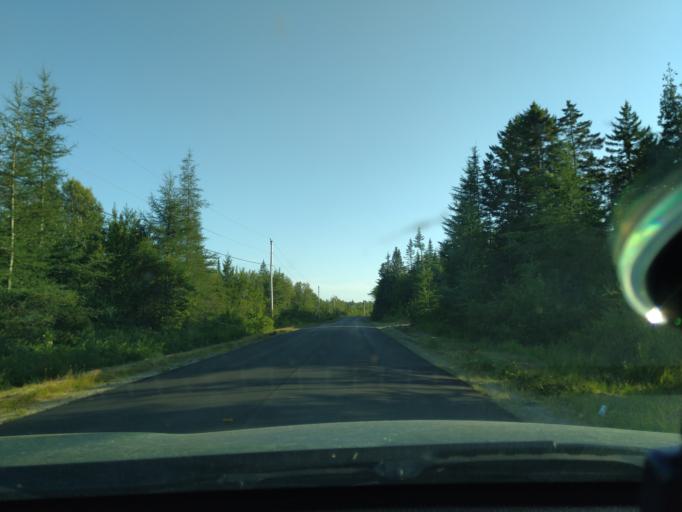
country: US
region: Maine
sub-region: Washington County
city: Machiasport
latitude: 44.6906
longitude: -67.1659
